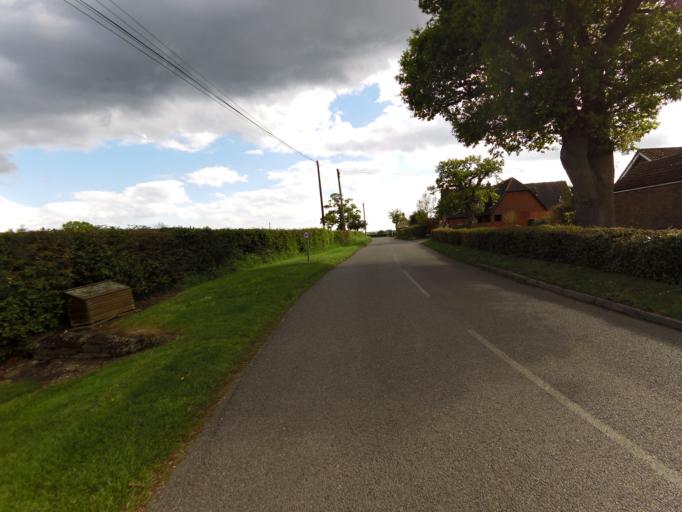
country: GB
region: England
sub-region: Suffolk
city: Elmswell
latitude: 52.2008
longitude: 0.9472
